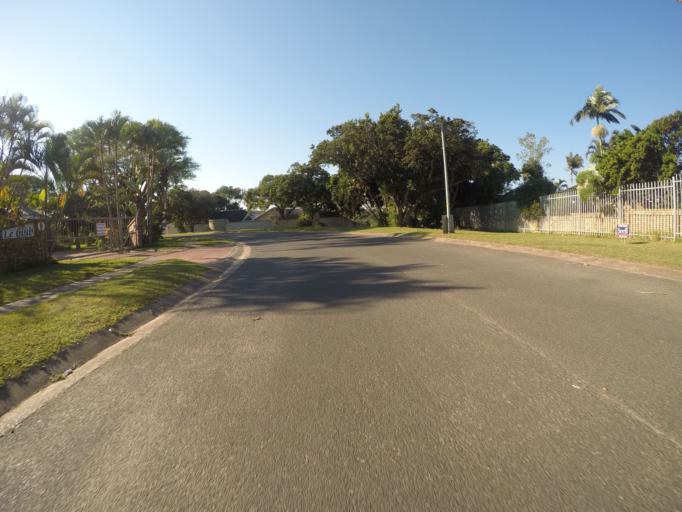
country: ZA
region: KwaZulu-Natal
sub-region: uThungulu District Municipality
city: Richards Bay
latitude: -28.7883
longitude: 32.1021
